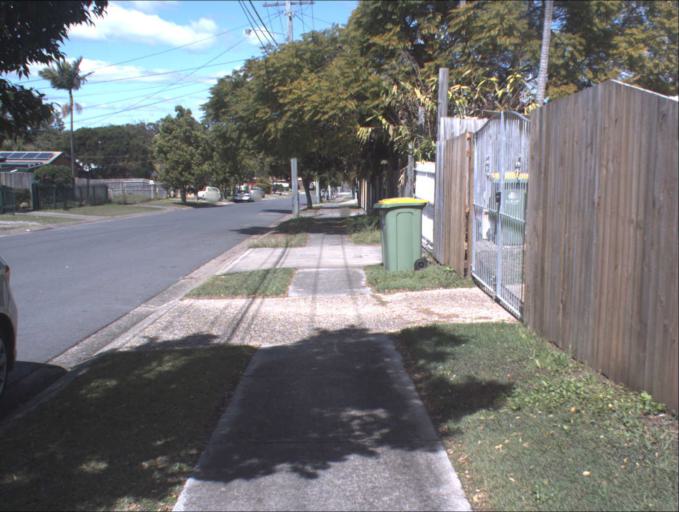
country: AU
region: Queensland
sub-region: Logan
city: Waterford West
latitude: -27.6886
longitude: 153.0983
